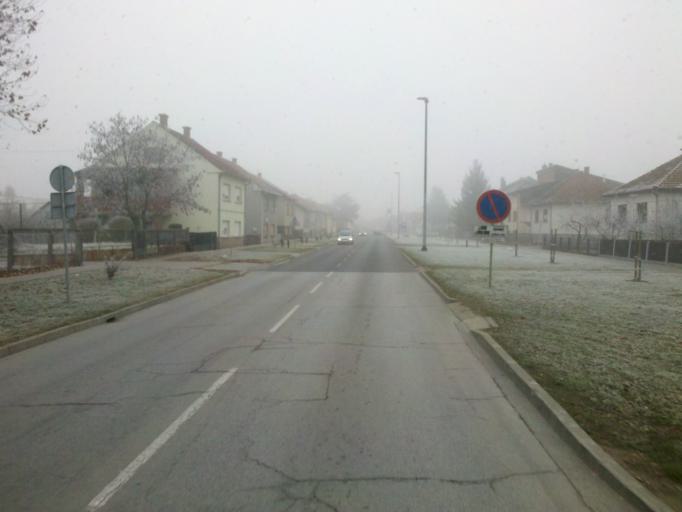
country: HR
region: Medimurska
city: Cakovec
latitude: 46.3793
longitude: 16.4272
